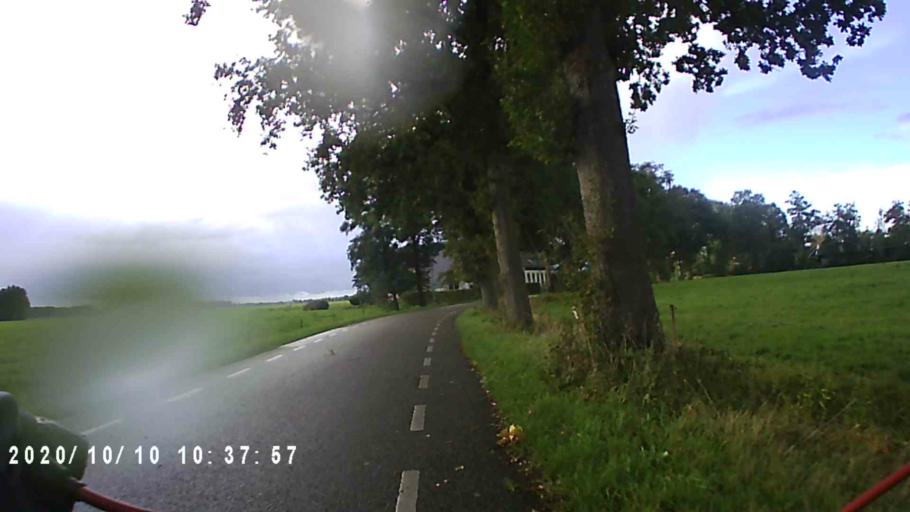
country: NL
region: Groningen
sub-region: Gemeente Grootegast
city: Grootegast
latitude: 53.1820
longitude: 6.2984
